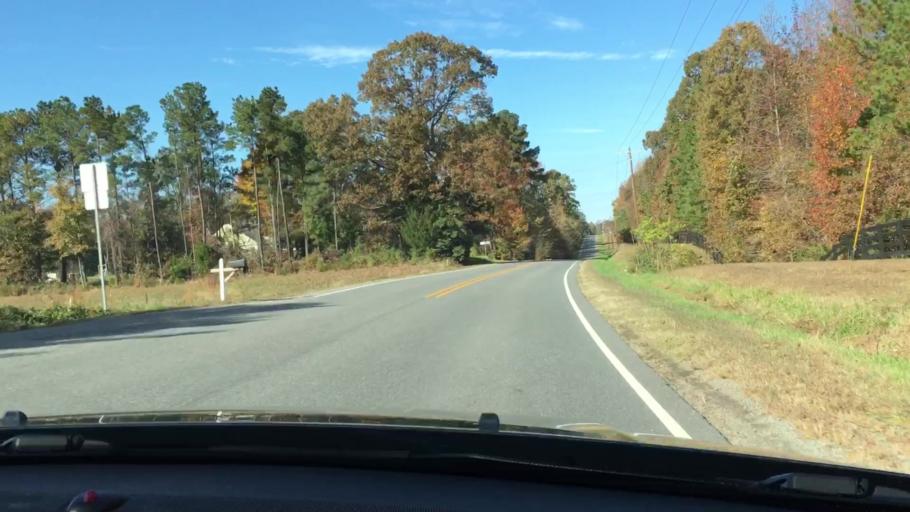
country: US
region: Virginia
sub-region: King and Queen County
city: King and Queen Court House
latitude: 37.5986
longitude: -76.9059
